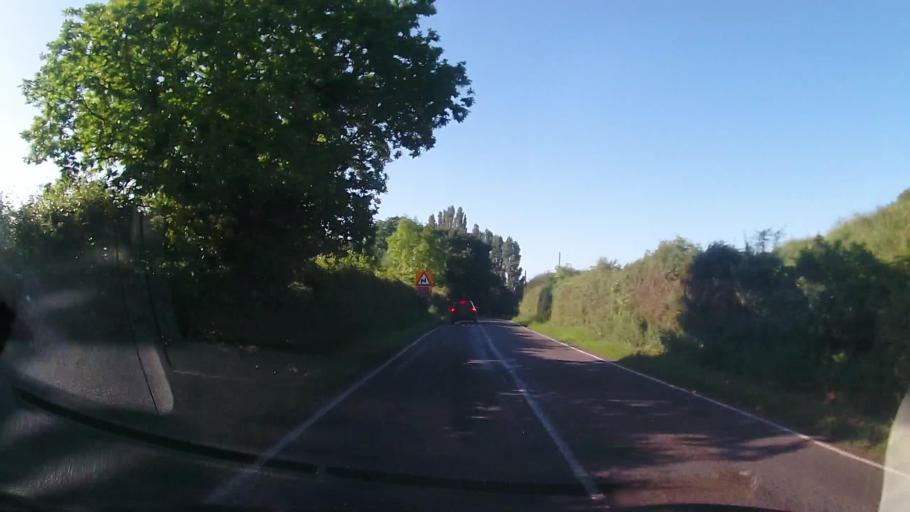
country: GB
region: England
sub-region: Shropshire
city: Shawbury
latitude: 52.7691
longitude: -2.6342
